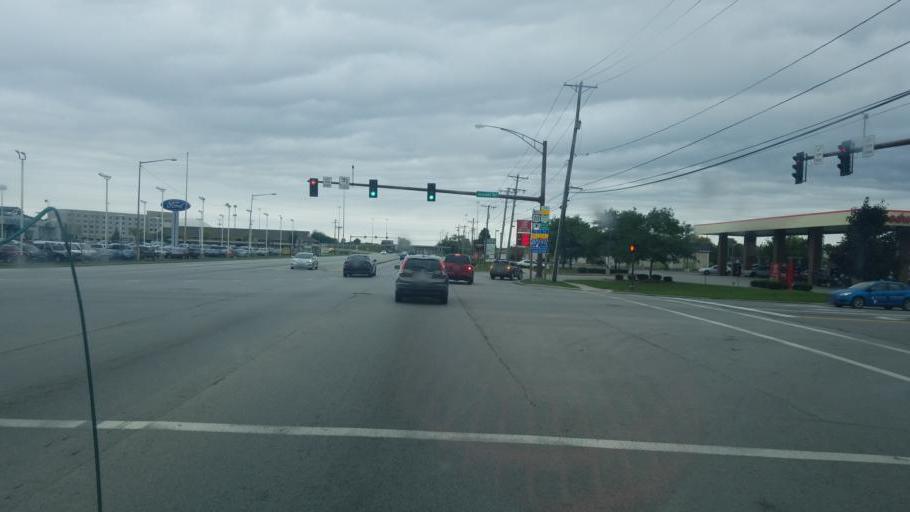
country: US
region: Ohio
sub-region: Lucas County
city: Maumee
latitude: 41.5852
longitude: -83.6648
